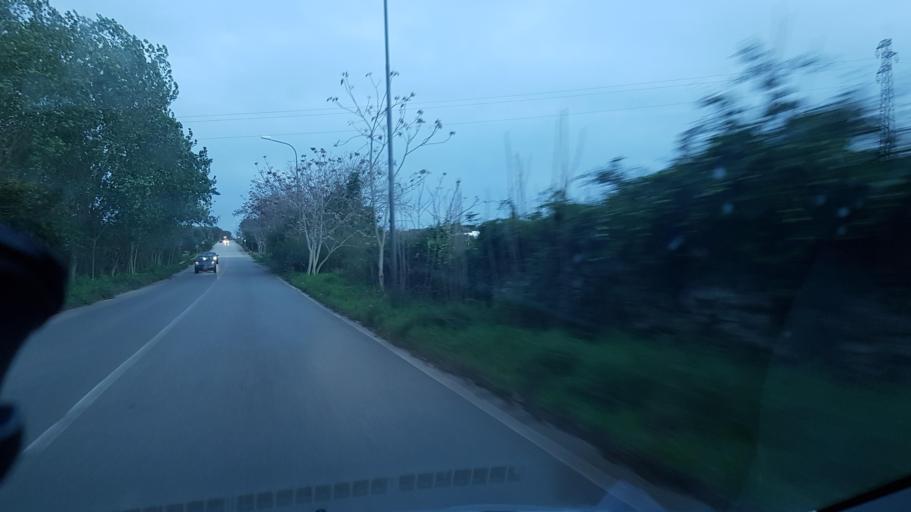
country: IT
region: Apulia
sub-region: Provincia di Brindisi
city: Ceglie Messapica
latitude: 40.6453
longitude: 17.5271
